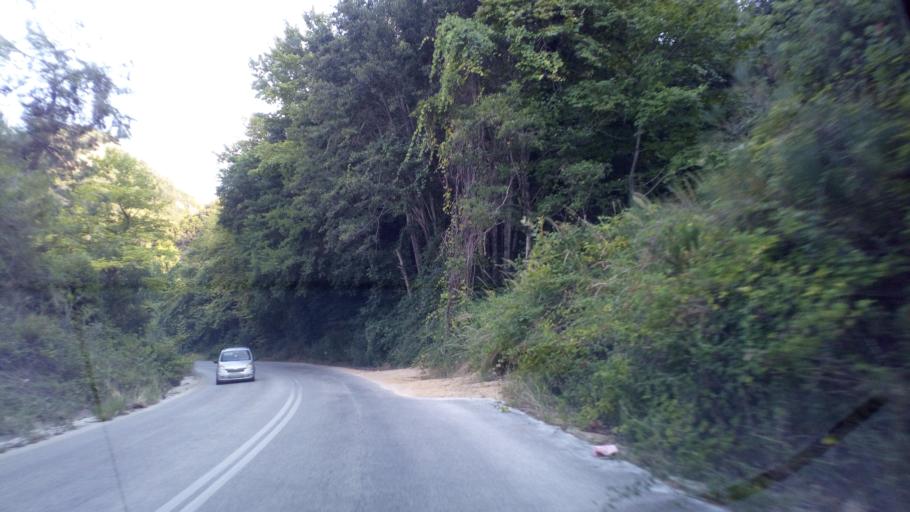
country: GR
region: Central Macedonia
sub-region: Nomos Chalkidikis
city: Neos Marmaras
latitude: 40.1711
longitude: 23.8506
